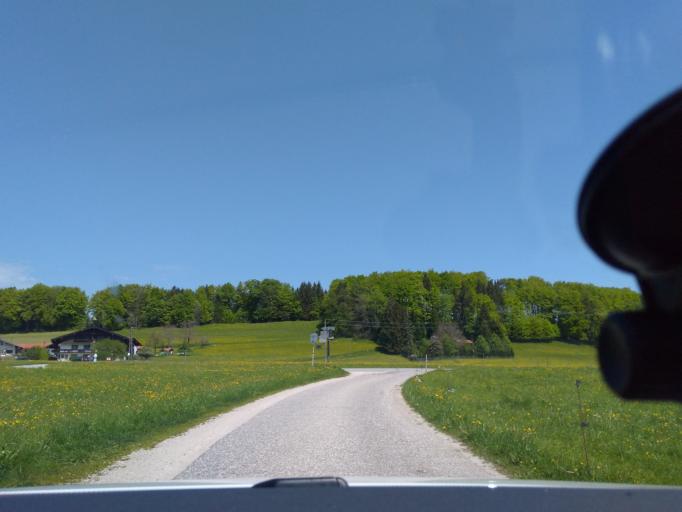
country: DE
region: Bavaria
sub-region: Upper Bavaria
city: Bernau am Chiemsee
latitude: 47.7863
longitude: 12.3612
